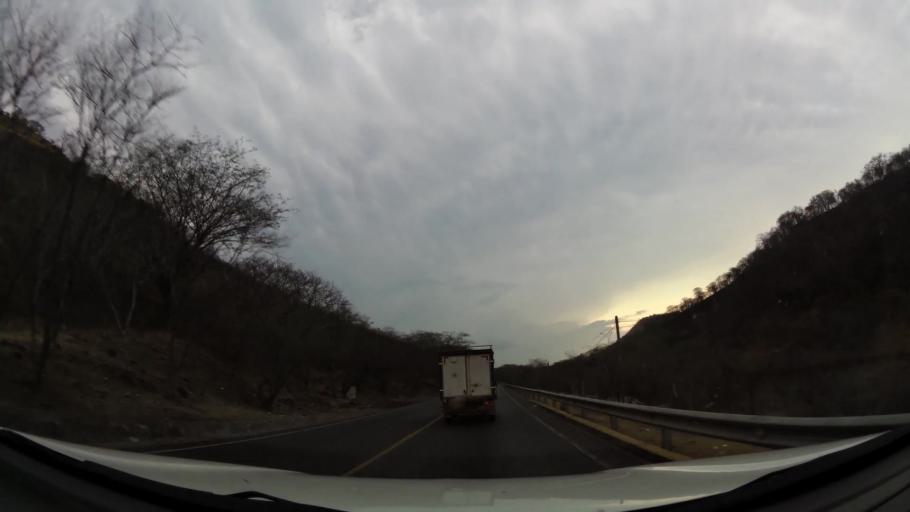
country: NI
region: Esteli
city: Esteli
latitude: 12.9453
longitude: -86.2203
